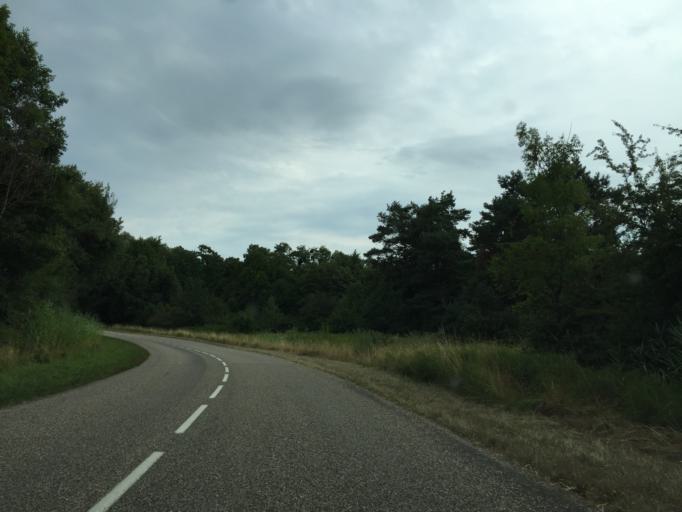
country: FR
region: Alsace
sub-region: Departement du Bas-Rhin
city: Soultz-sous-Forets
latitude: 48.9969
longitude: 7.8774
